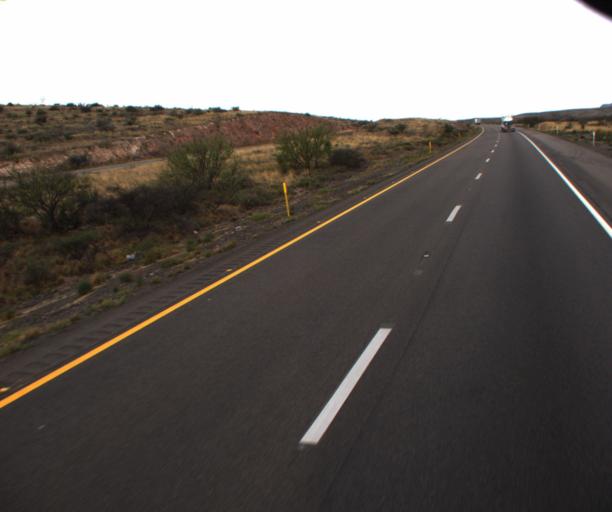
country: US
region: Arizona
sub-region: Cochise County
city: Willcox
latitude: 32.1507
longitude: -109.9924
